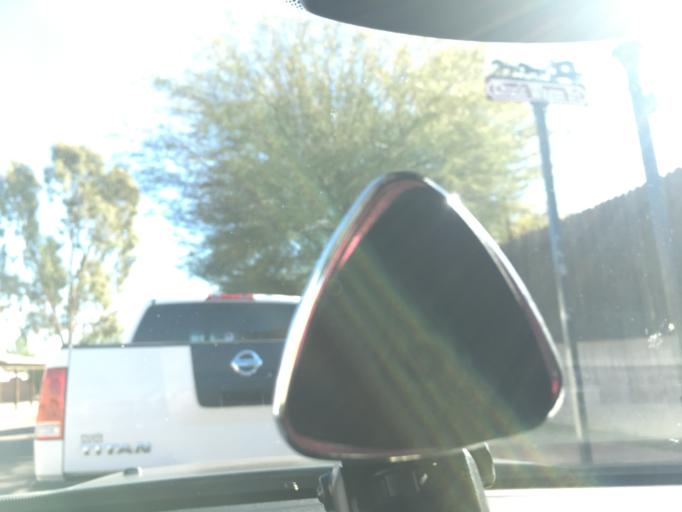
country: US
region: Arizona
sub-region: Maricopa County
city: Wickenburg
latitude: 33.9686
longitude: -112.7298
